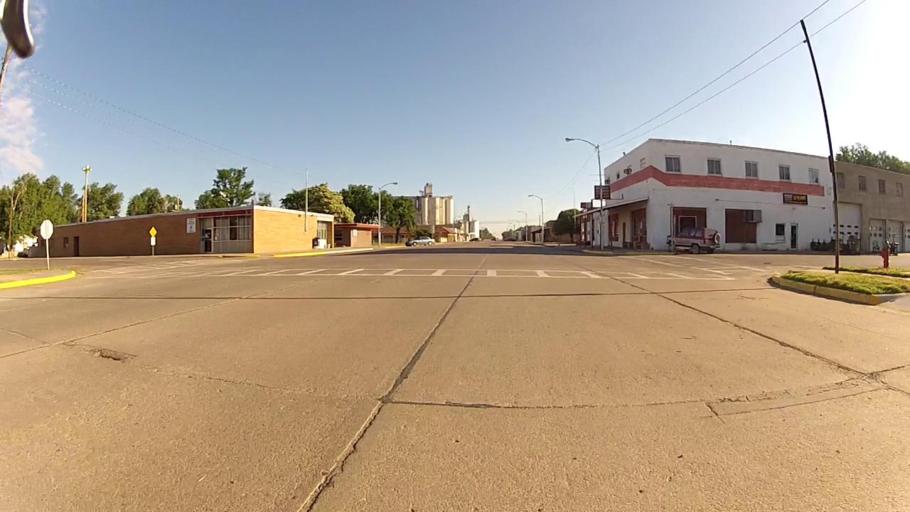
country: US
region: Kansas
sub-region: Haskell County
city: Sublette
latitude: 37.4799
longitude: -100.8438
